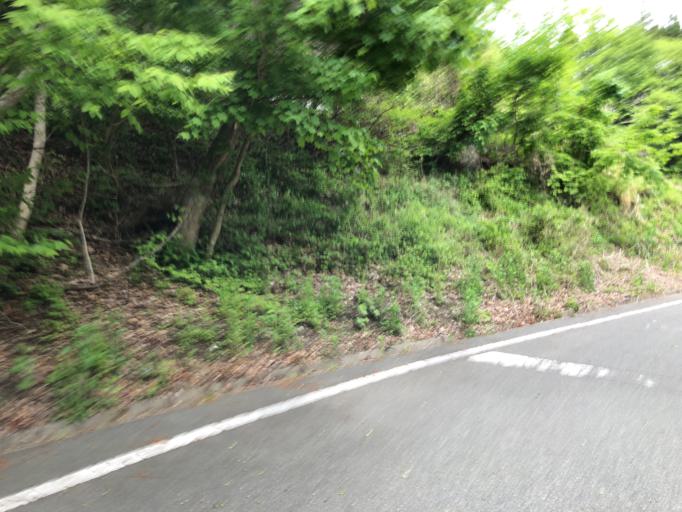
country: JP
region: Miyagi
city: Marumori
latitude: 37.7217
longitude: 140.7861
